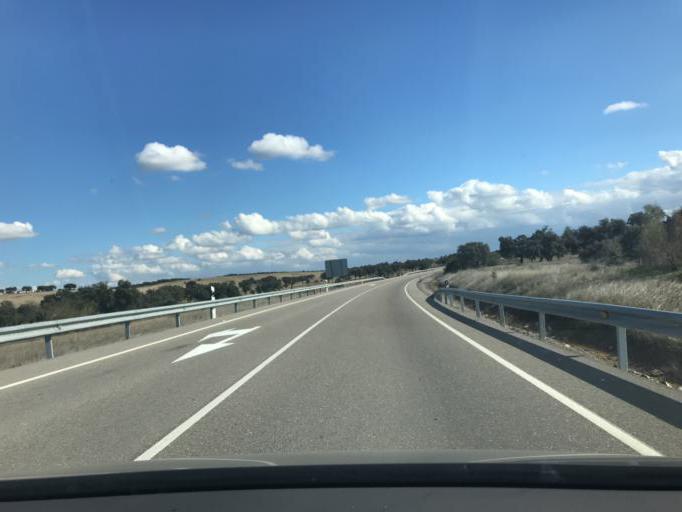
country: ES
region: Extremadura
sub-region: Provincia de Badajoz
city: Granja de Torrehermosa
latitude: 38.2880
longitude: -5.5249
